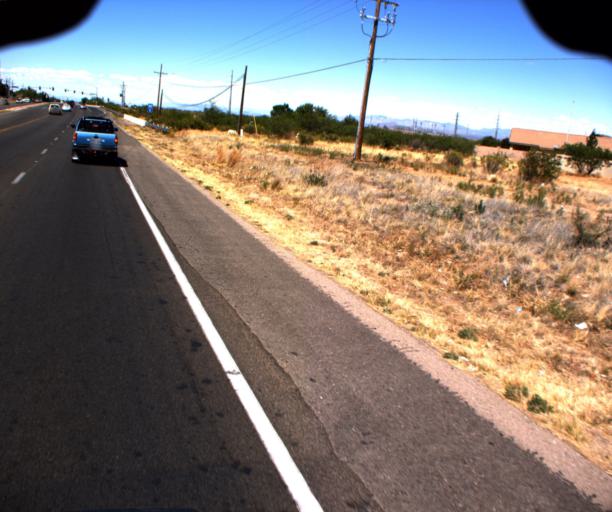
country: US
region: Arizona
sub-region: Cochise County
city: Sierra Vista
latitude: 31.5081
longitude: -110.2573
